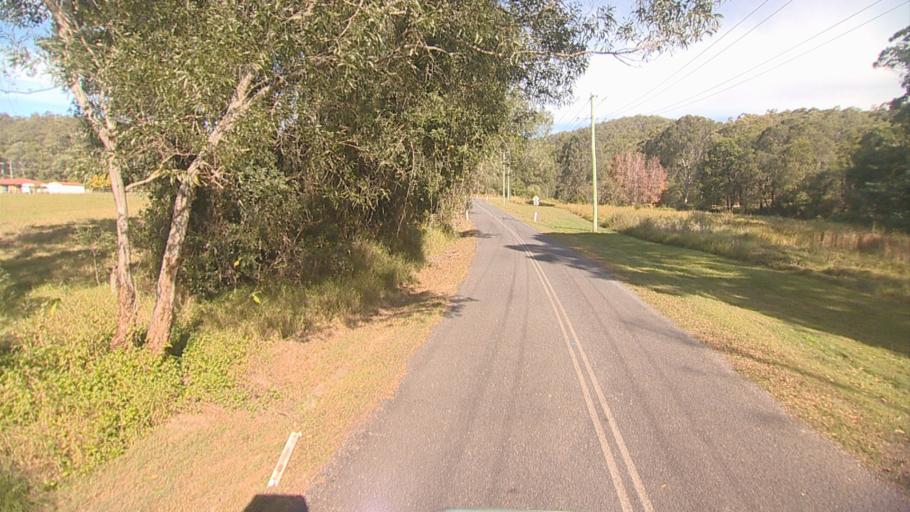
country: AU
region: Queensland
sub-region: Logan
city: Windaroo
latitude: -27.7763
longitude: 153.1800
